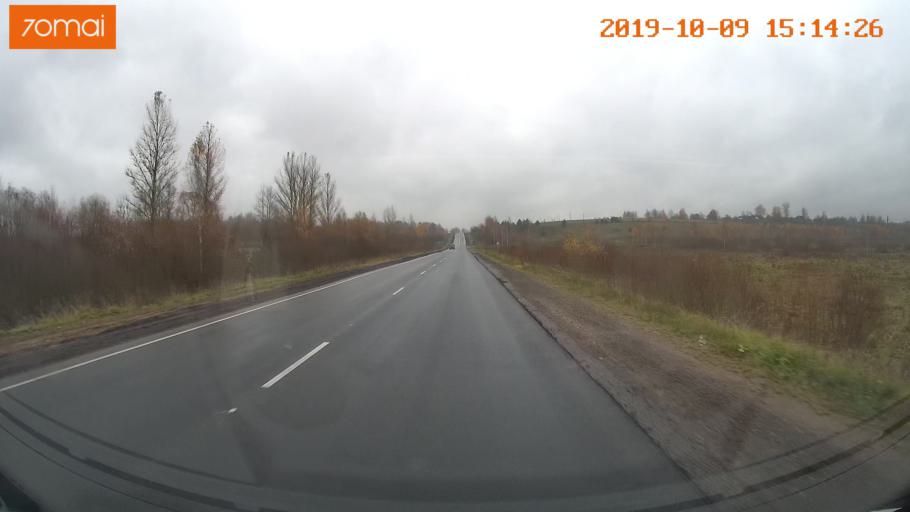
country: RU
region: Kostroma
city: Susanino
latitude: 58.1346
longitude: 41.6021
